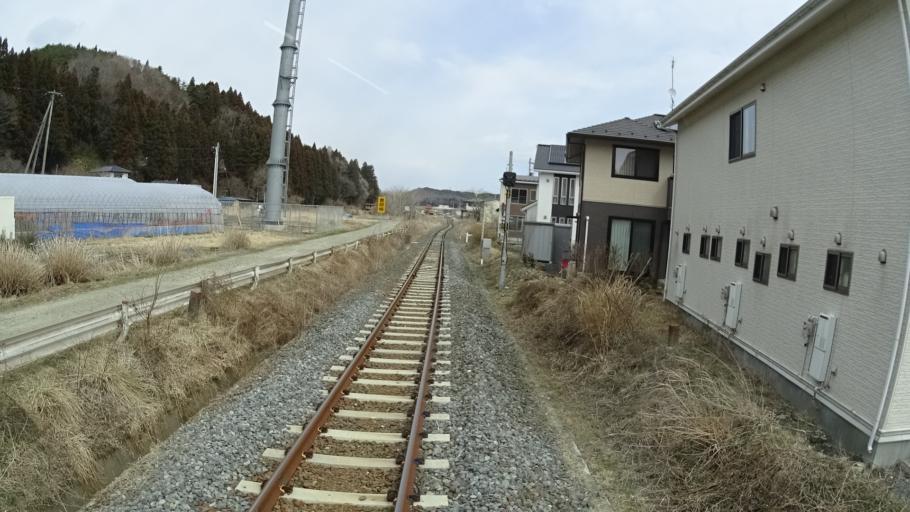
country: JP
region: Iwate
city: Yamada
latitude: 39.5324
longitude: 141.9243
